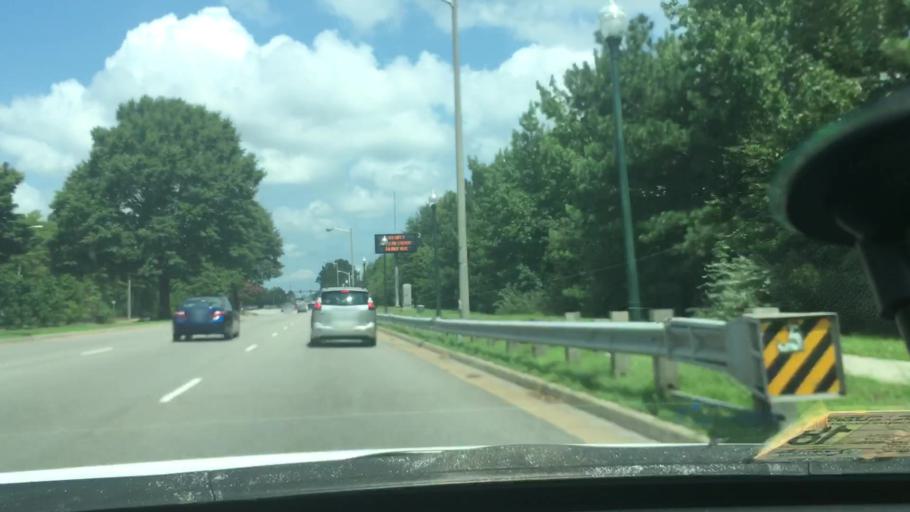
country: US
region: Virginia
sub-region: City of Chesapeake
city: Chesapeake
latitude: 36.7722
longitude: -76.2287
